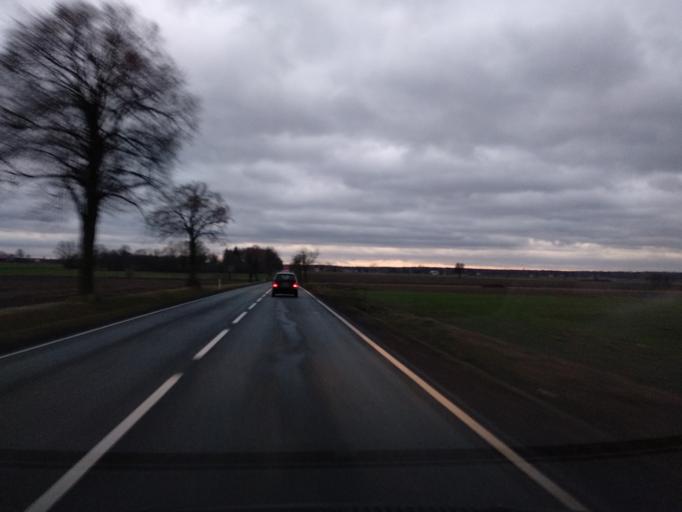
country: PL
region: Greater Poland Voivodeship
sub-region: Powiat koninski
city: Rychwal
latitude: 52.0504
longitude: 18.1627
